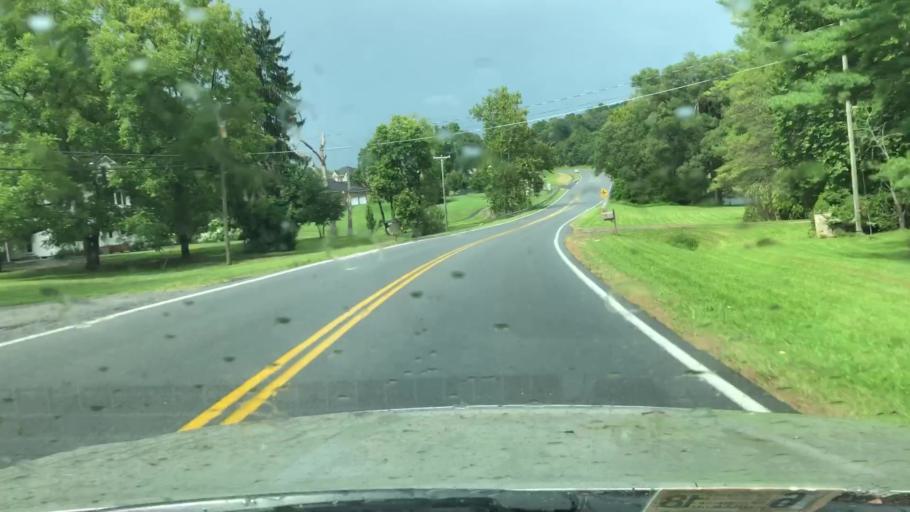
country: US
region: Virginia
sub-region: City of Waynesboro
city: Waynesboro
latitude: 38.0887
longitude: -78.9014
